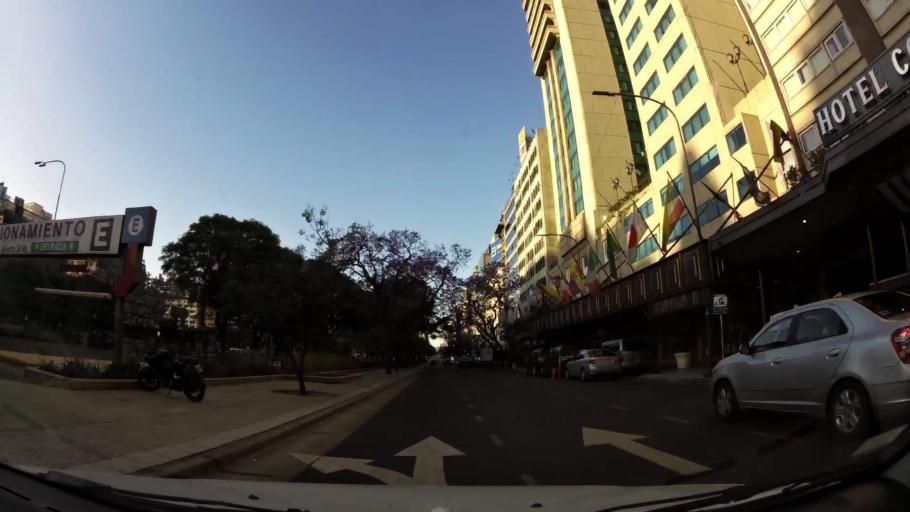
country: AR
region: Buenos Aires F.D.
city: Buenos Aires
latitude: -34.6023
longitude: -58.3811
